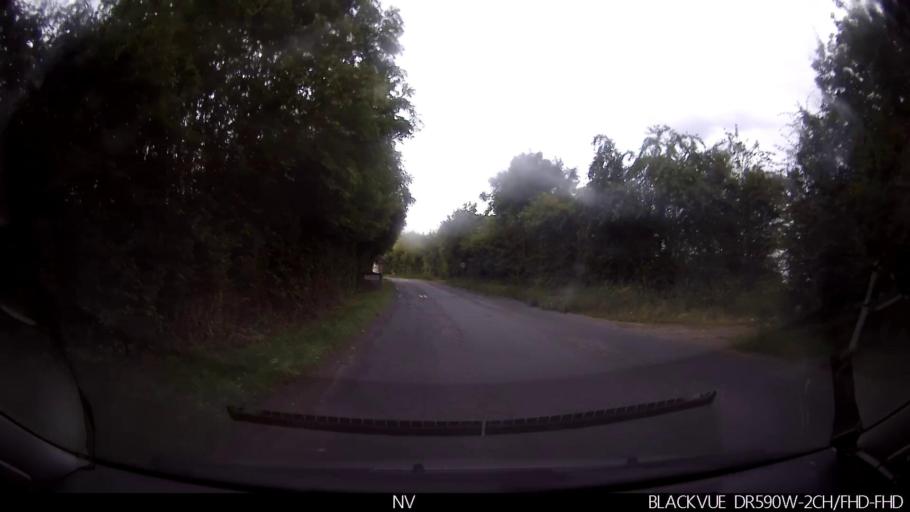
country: GB
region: England
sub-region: City of York
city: Holtby
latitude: 54.0478
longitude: -0.9591
